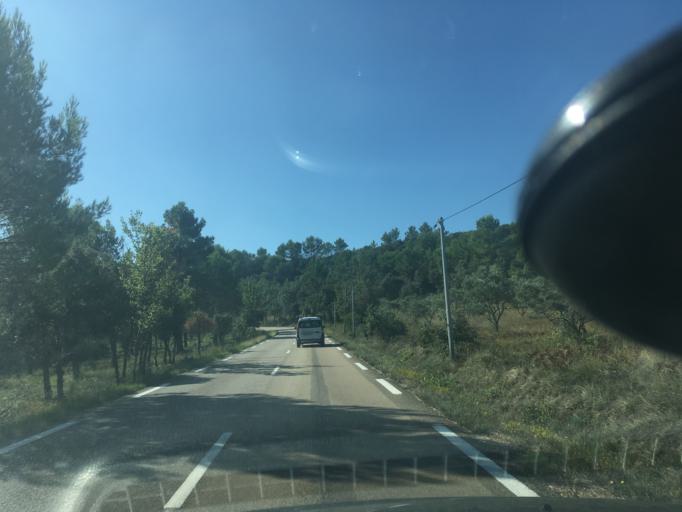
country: FR
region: Provence-Alpes-Cote d'Azur
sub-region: Departement du Var
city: Barjols
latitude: 43.6070
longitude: 6.0686
